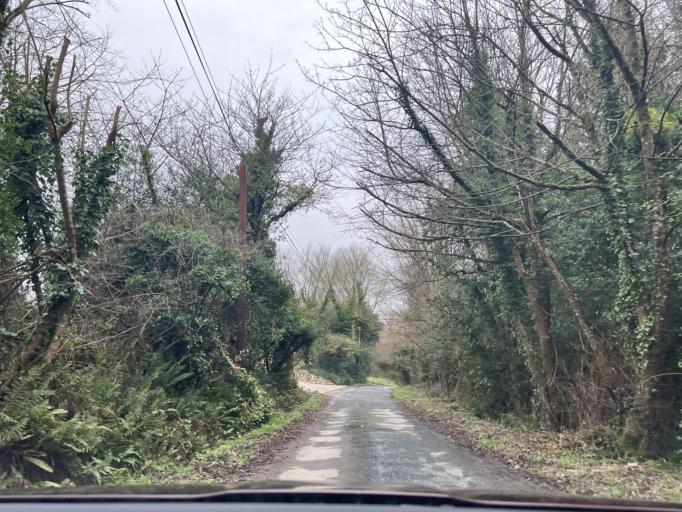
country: IE
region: Leinster
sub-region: Loch Garman
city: Castlebridge
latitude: 52.3857
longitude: -6.5527
